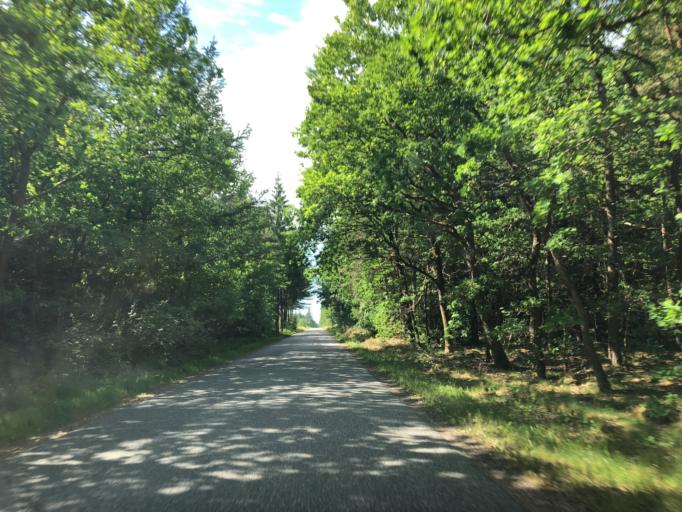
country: DK
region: Central Jutland
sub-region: Herning Kommune
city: Lind
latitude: 56.0254
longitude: 8.9600
